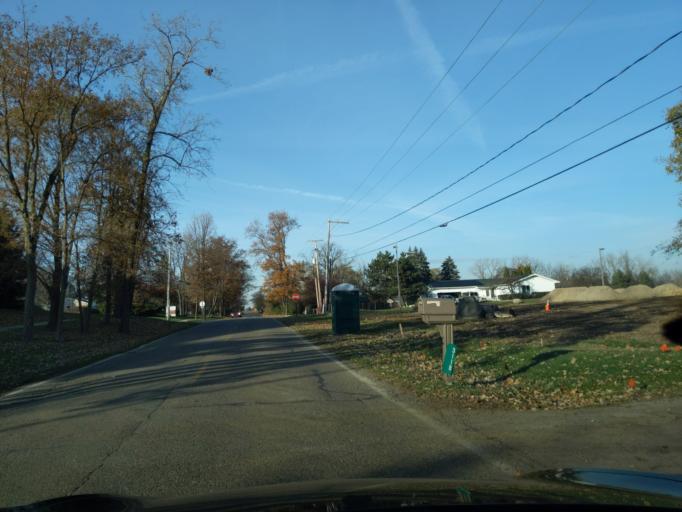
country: US
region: Michigan
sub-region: Ingham County
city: East Lansing
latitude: 42.7651
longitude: -84.5084
